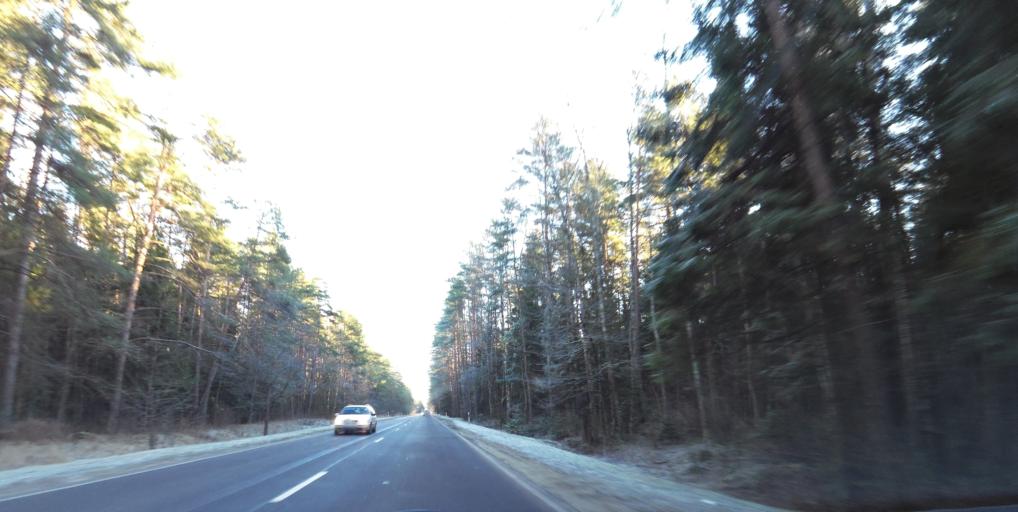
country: LT
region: Vilnius County
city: Lazdynai
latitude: 54.6431
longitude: 25.1652
